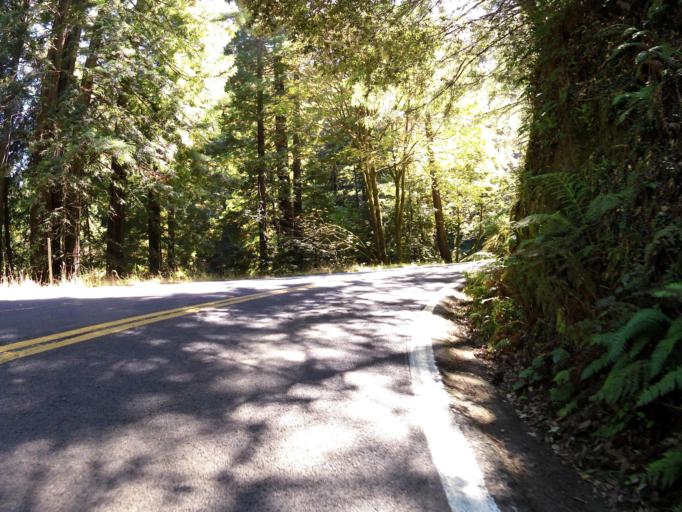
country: US
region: California
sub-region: Mendocino County
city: Fort Bragg
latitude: 39.7342
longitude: -123.8104
